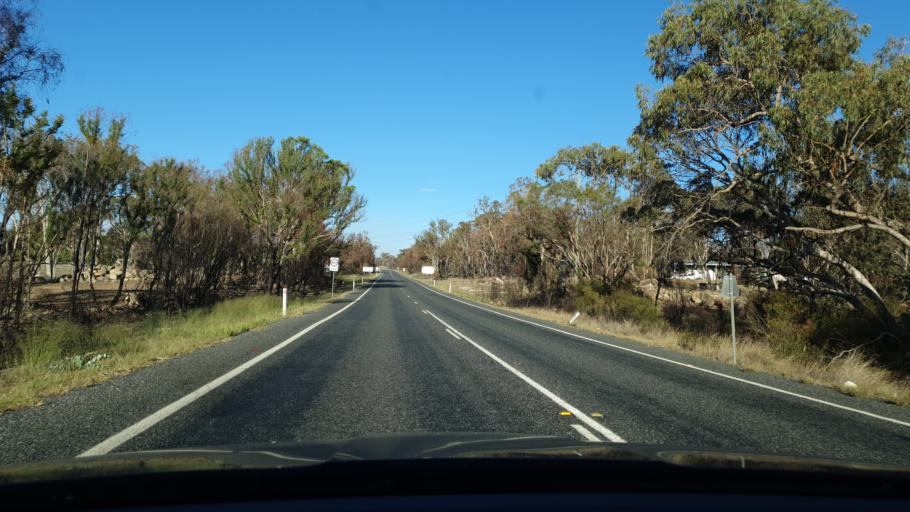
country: AU
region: Queensland
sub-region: Southern Downs
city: Stanthorpe
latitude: -28.6399
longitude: 151.9419
